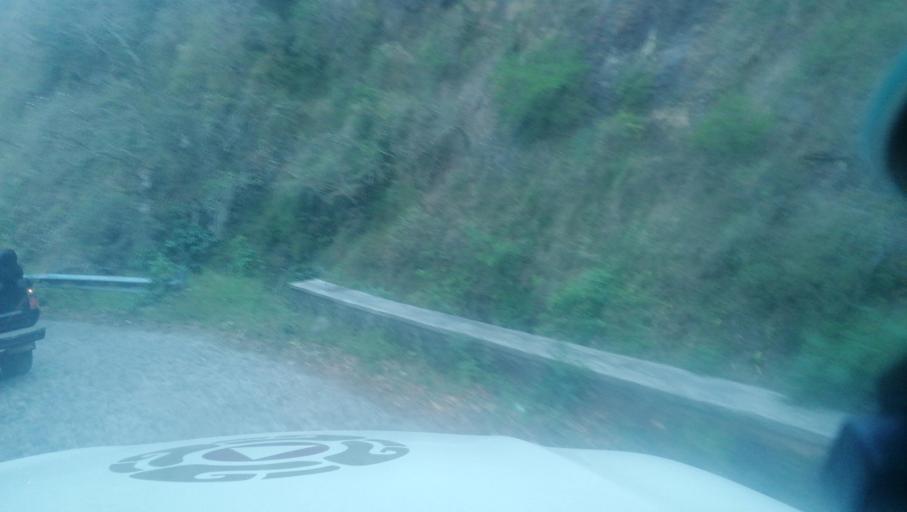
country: MX
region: Chiapas
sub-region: Cacahoatan
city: Benito Juarez
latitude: 15.1420
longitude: -92.1969
